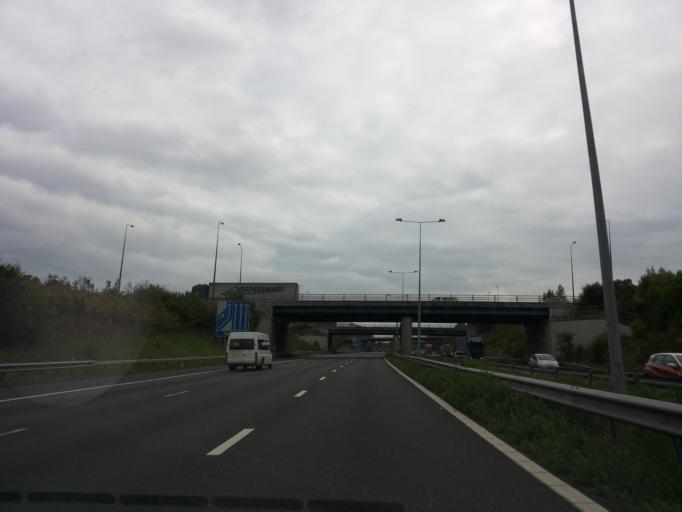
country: GB
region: England
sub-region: Kent
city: Aylesford
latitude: 51.3363
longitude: 0.5091
